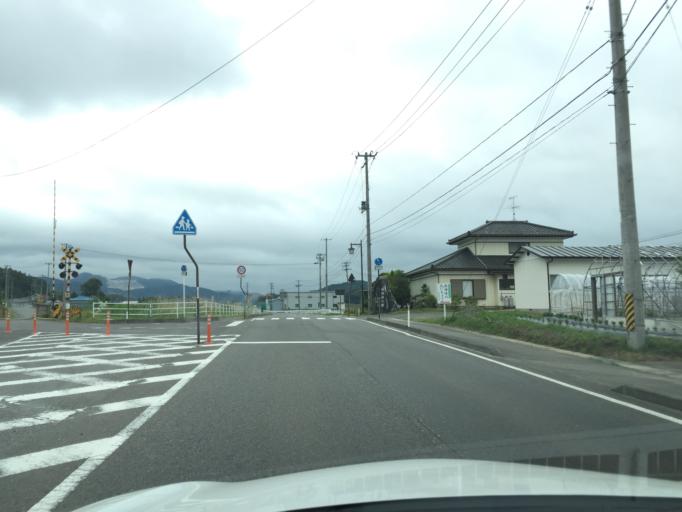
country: JP
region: Fukushima
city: Funehikimachi-funehiki
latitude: 37.4104
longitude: 140.6107
